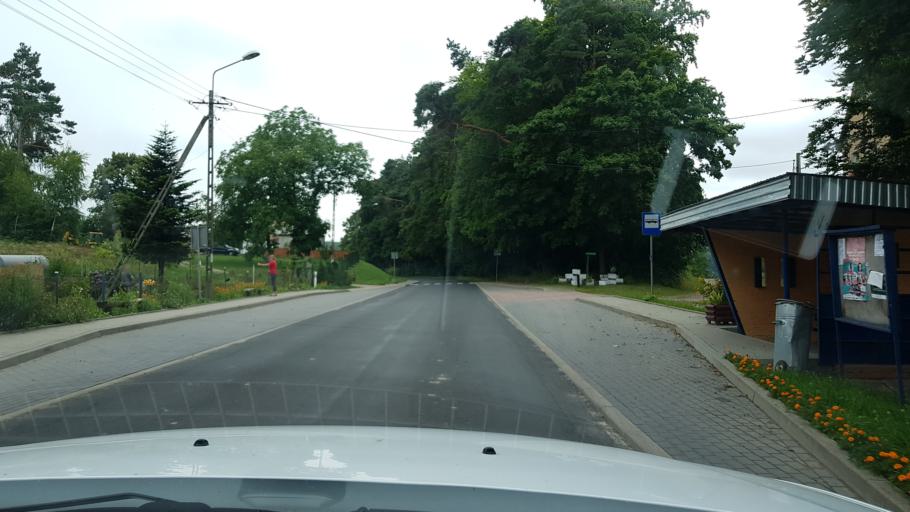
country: PL
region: West Pomeranian Voivodeship
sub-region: Powiat slawienski
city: Slawno
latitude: 54.4869
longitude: 16.5834
